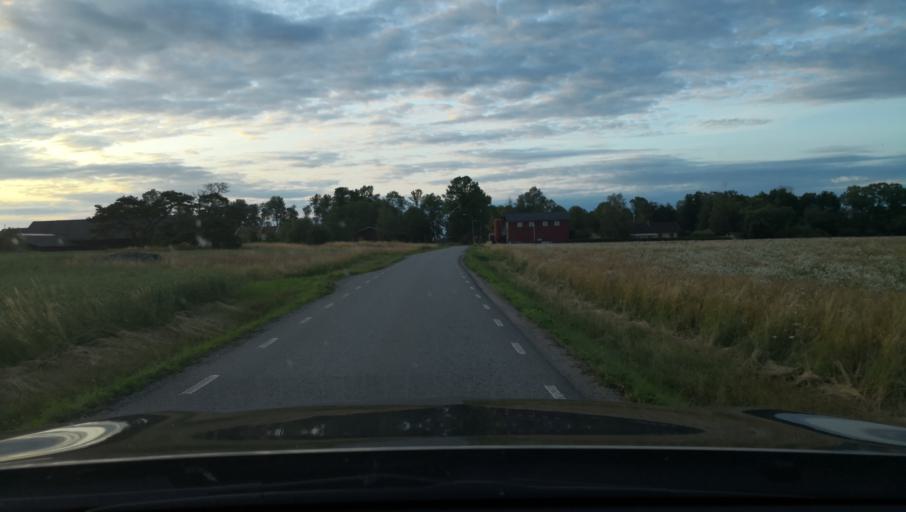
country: SE
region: Uppsala
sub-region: Uppsala Kommun
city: Vattholma
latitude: 60.0355
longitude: 17.6645
